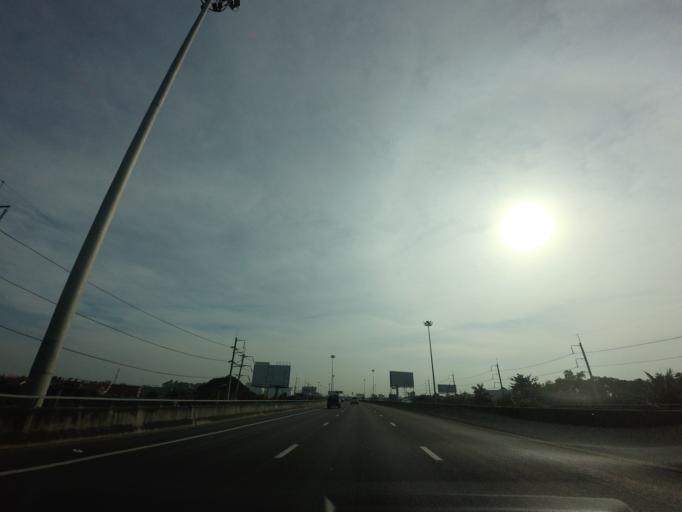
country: TH
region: Bangkok
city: Lat Phrao
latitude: 13.8328
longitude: 100.6306
